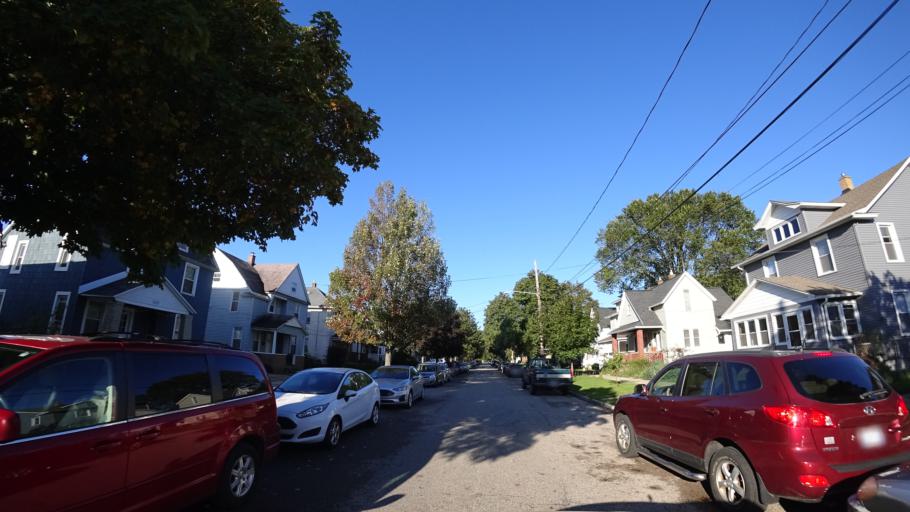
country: US
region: Michigan
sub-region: Kent County
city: Grand Rapids
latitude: 42.9619
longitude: -85.6950
